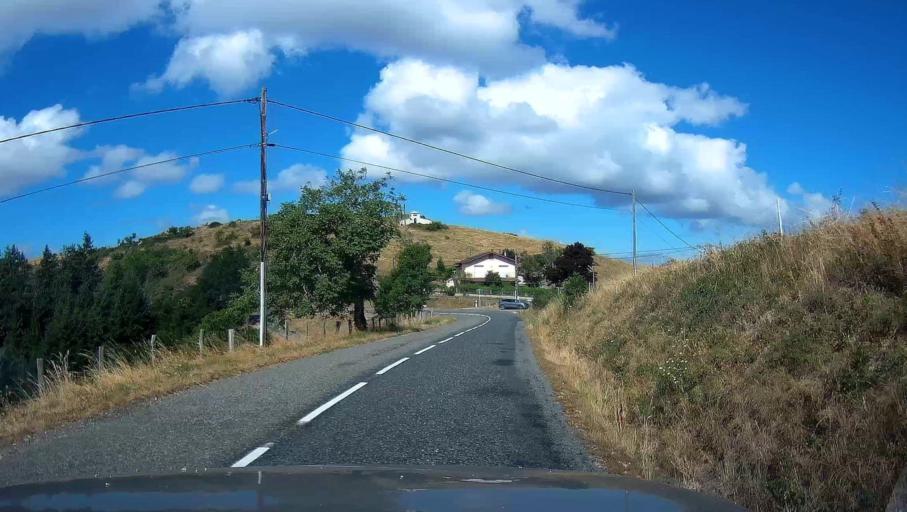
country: FR
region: Rhone-Alpes
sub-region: Departement du Rhone
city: Grandris
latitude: 46.0043
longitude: 4.5367
